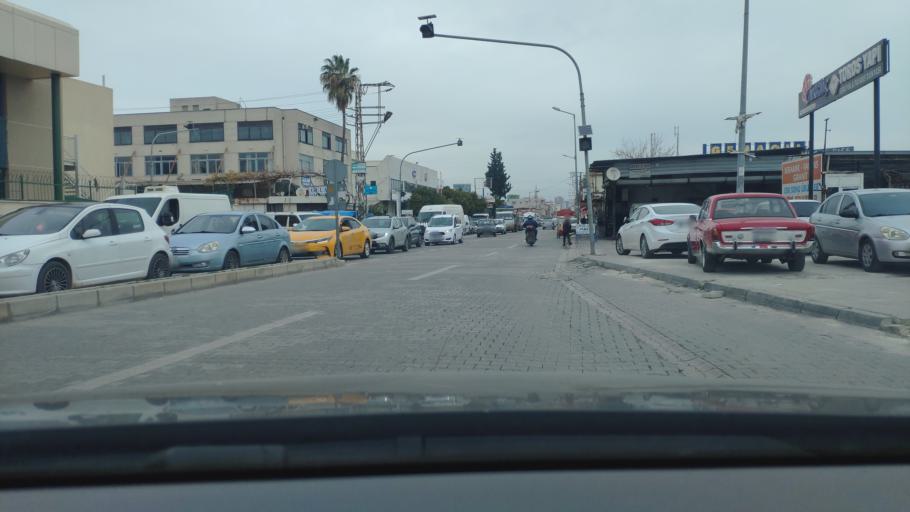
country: TR
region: Adana
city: Seyhan
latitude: 36.9947
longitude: 35.2878
